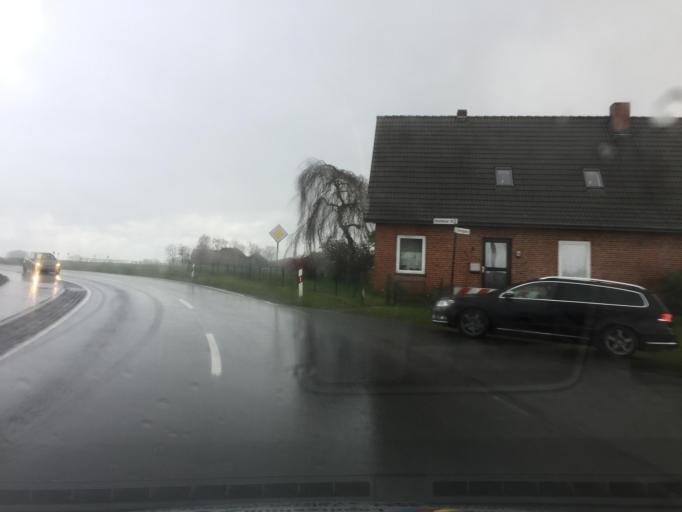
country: DE
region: Lower Saxony
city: Sustedt
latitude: 52.9220
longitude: 8.8884
